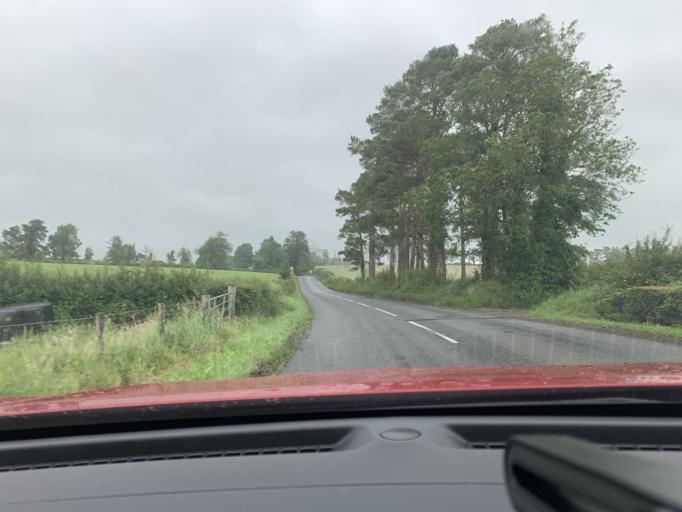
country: GB
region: Northern Ireland
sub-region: Fermanagh District
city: Enniskillen
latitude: 54.3099
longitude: -7.6840
